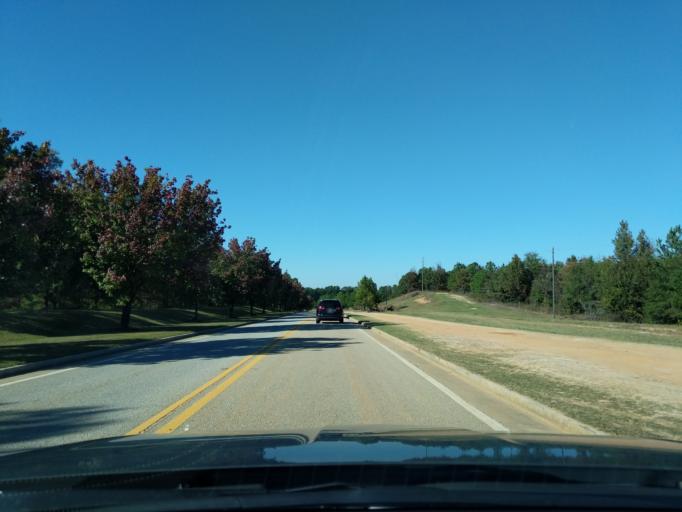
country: US
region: Georgia
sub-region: Columbia County
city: Grovetown
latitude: 33.4626
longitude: -82.1824
